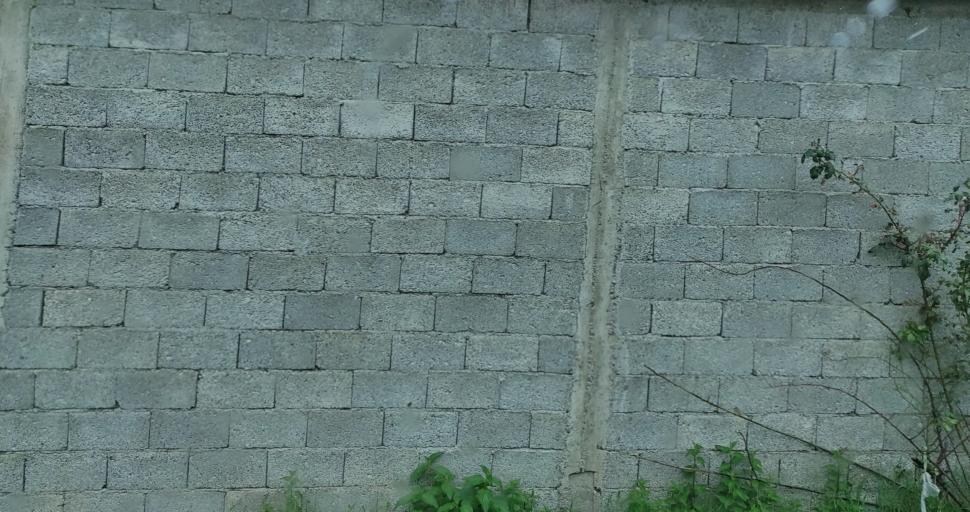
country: AL
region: Shkoder
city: Vukatane
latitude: 41.9998
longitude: 19.5505
